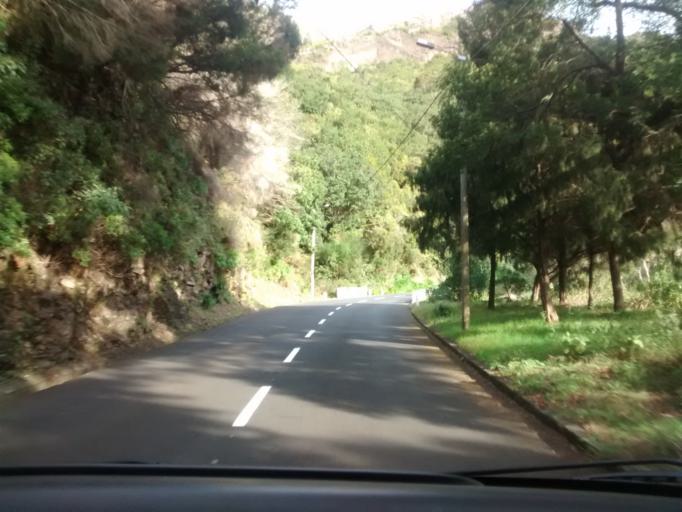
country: PT
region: Madeira
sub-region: Sao Vicente
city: Sao Vicente
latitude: 32.7518
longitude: -17.0246
